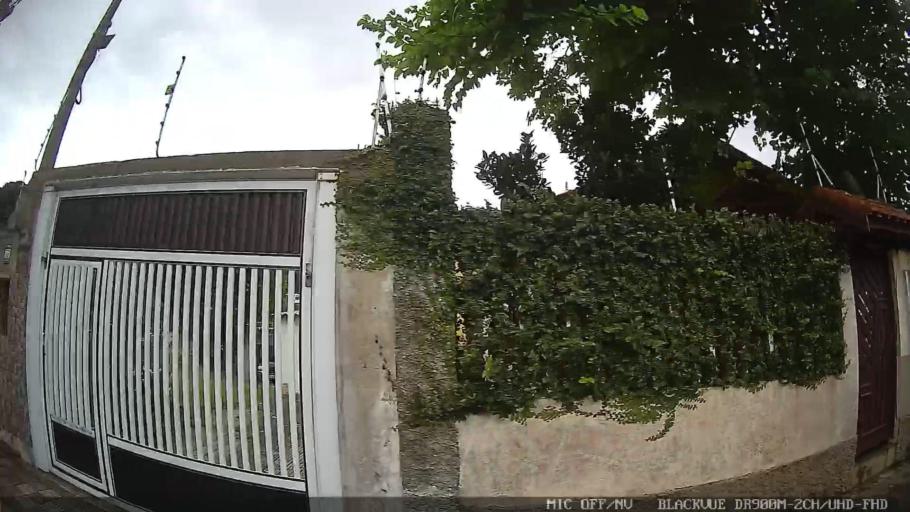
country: BR
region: Sao Paulo
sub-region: Itanhaem
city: Itanhaem
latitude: -24.1931
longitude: -46.8026
